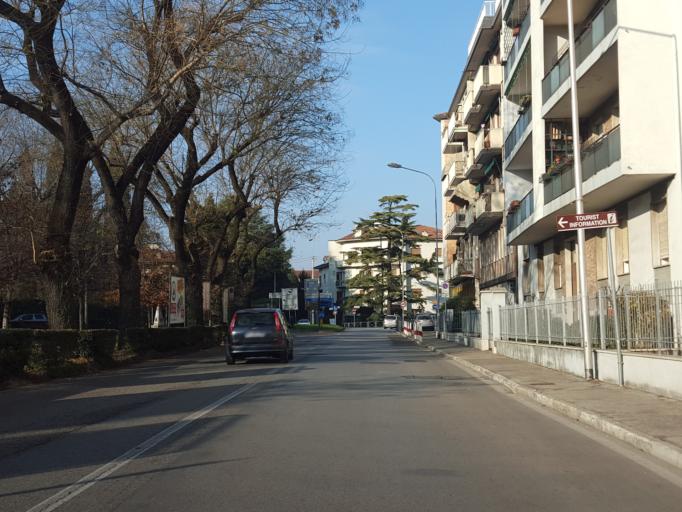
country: IT
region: Veneto
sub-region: Provincia di Vicenza
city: Vicenza
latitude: 45.5464
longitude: 11.5541
